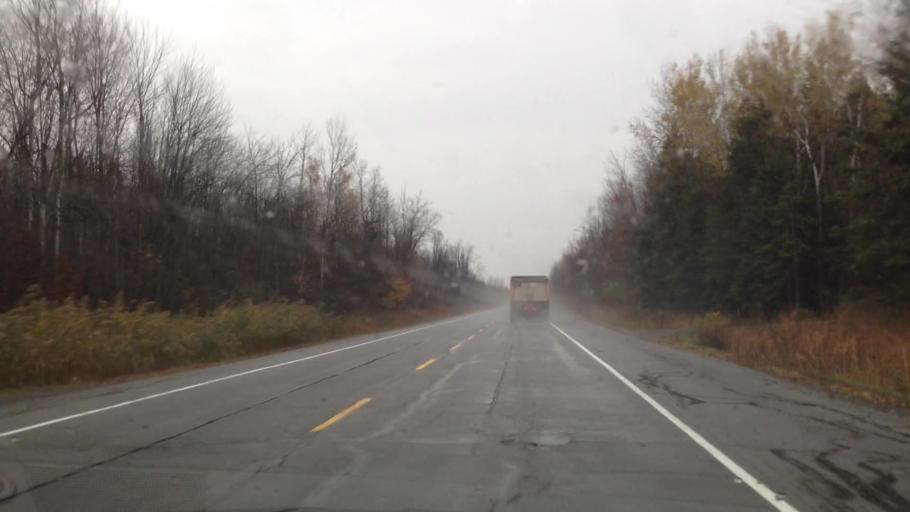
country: CA
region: Ontario
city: Clarence-Rockland
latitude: 45.3624
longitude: -75.3745
